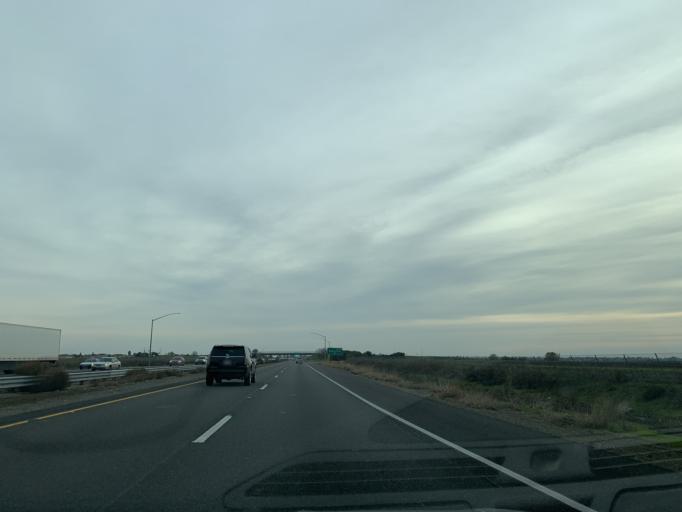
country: US
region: California
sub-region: Sacramento County
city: Elverta
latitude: 38.6913
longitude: -121.5403
